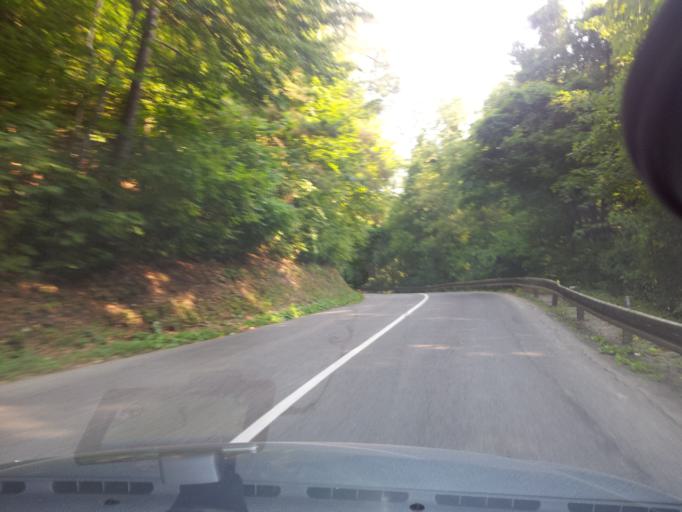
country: SK
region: Nitriansky
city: Trencianske Teplice
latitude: 48.8942
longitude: 18.1756
